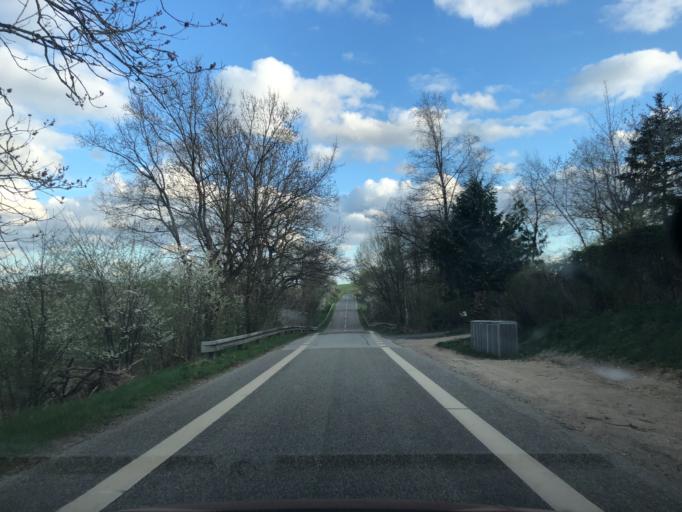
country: DK
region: Zealand
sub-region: Lejre Kommune
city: Kirke Hvalso
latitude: 55.5128
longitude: 11.8673
